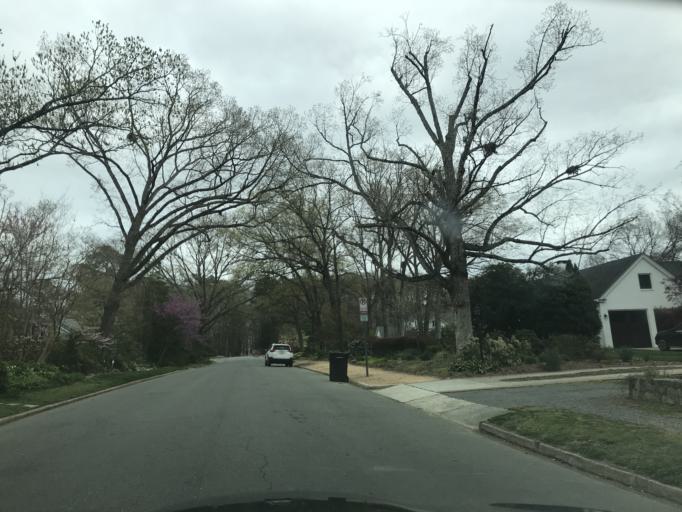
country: US
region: North Carolina
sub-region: Orange County
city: Chapel Hill
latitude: 35.9125
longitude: -79.0391
